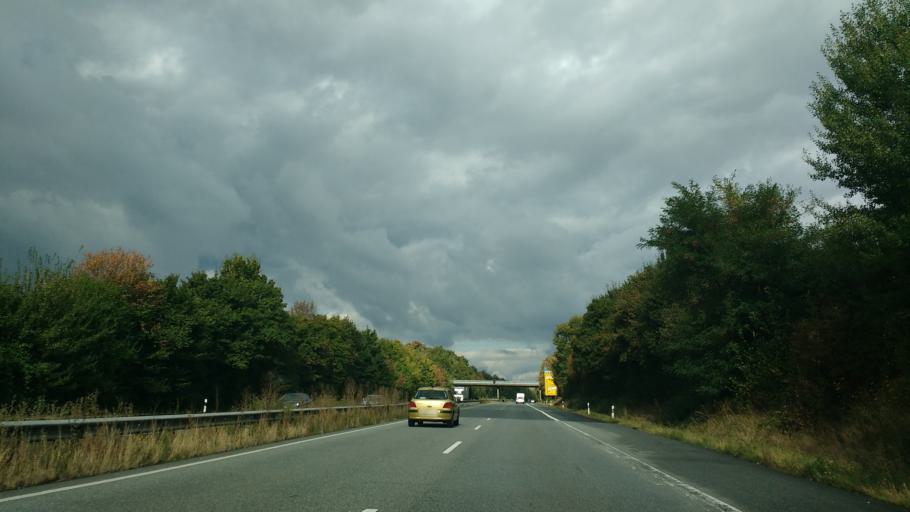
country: DE
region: North Rhine-Westphalia
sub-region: Regierungsbezirk Detmold
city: Herford
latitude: 52.1141
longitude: 8.6431
